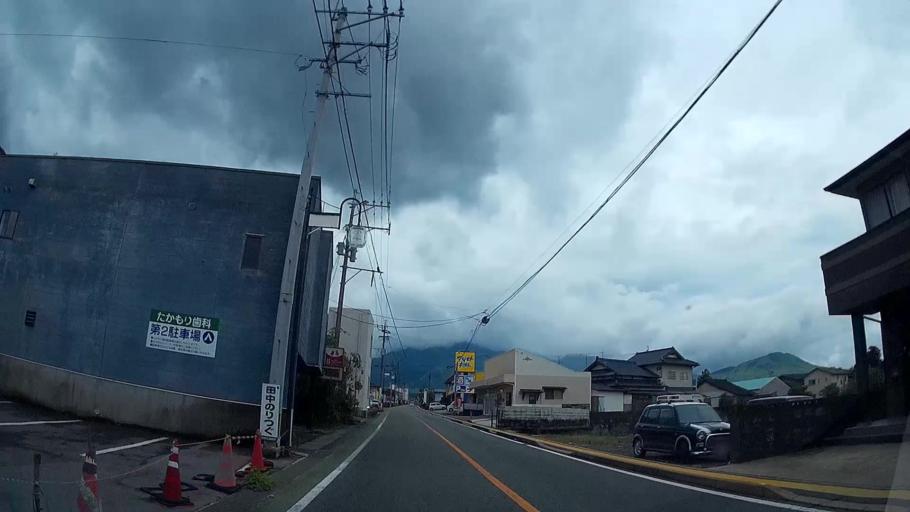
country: JP
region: Kumamoto
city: Aso
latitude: 32.9452
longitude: 131.1179
